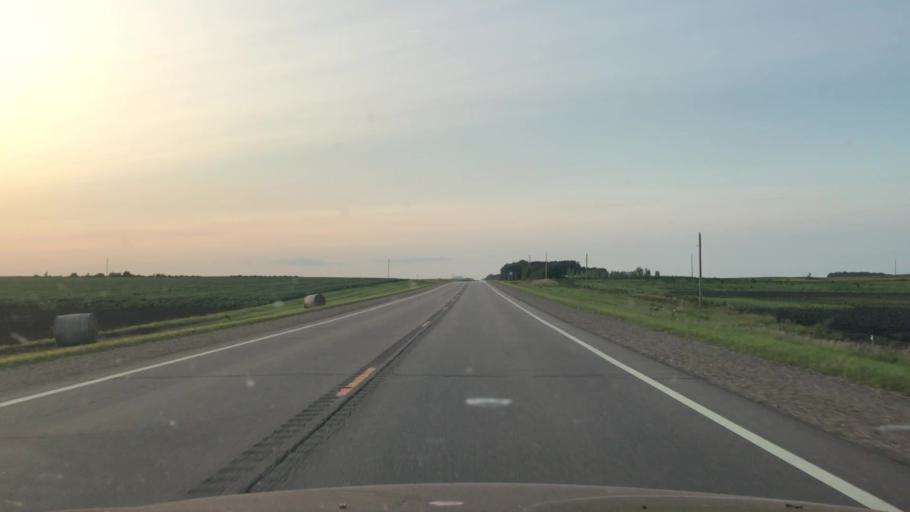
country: US
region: Minnesota
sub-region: Redwood County
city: Redwood Falls
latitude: 44.4386
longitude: -95.1176
